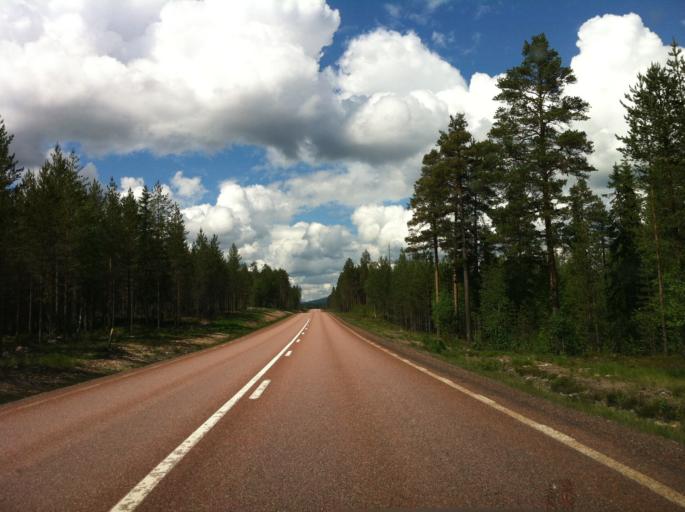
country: SE
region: Dalarna
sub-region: Malung-Saelens kommun
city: Malung
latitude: 60.7907
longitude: 13.4451
